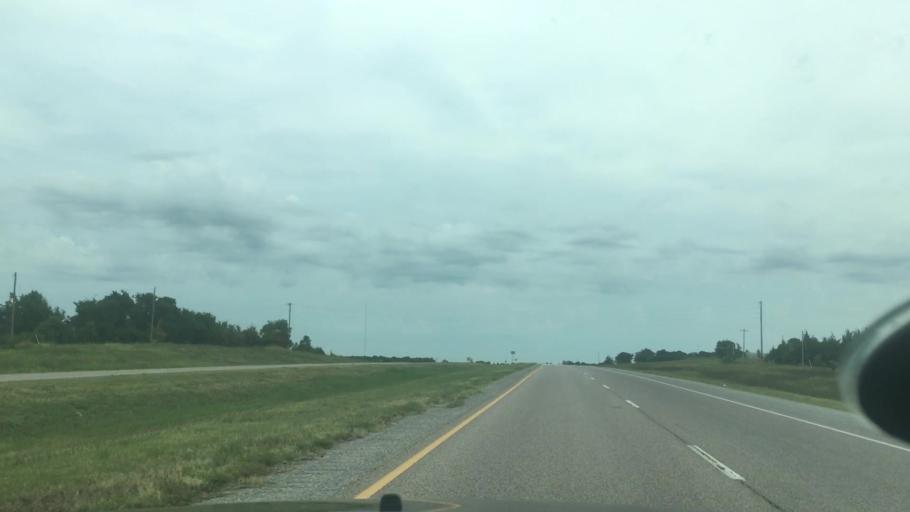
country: US
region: Oklahoma
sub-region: Pontotoc County
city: Byng
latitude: 34.8724
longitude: -96.6782
